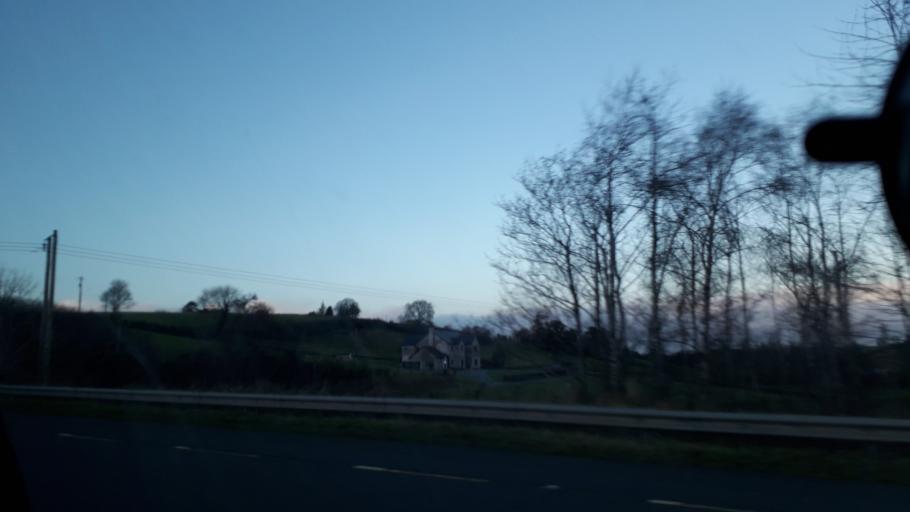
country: IE
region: Ulster
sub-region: County Monaghan
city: Monaghan
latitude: 54.2376
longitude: -6.9218
